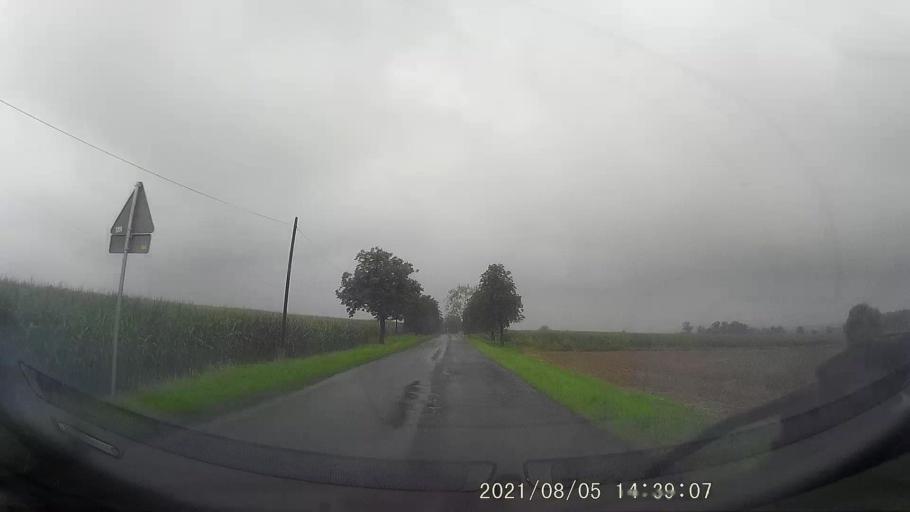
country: PL
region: Opole Voivodeship
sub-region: Powiat nyski
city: Sidzina
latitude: 50.4731
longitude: 17.4503
